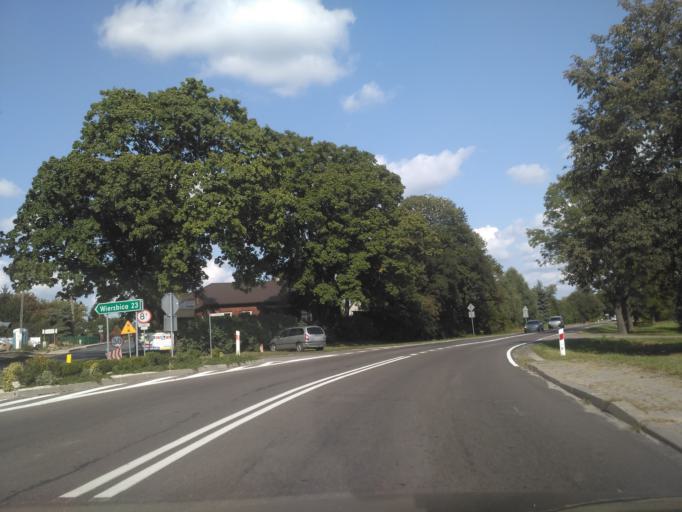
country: PL
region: Lublin Voivodeship
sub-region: Powiat chelmski
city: Rejowiec
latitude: 51.0972
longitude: 23.2853
